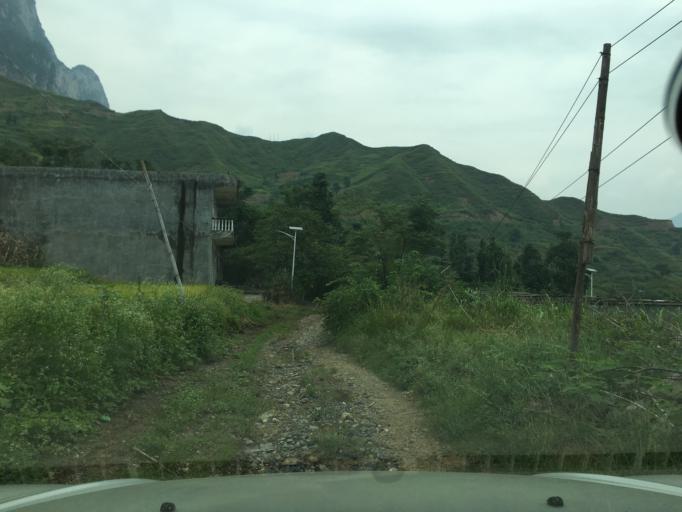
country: CN
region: Guizhou Sheng
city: Liupanshui
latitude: 26.0349
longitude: 105.1882
